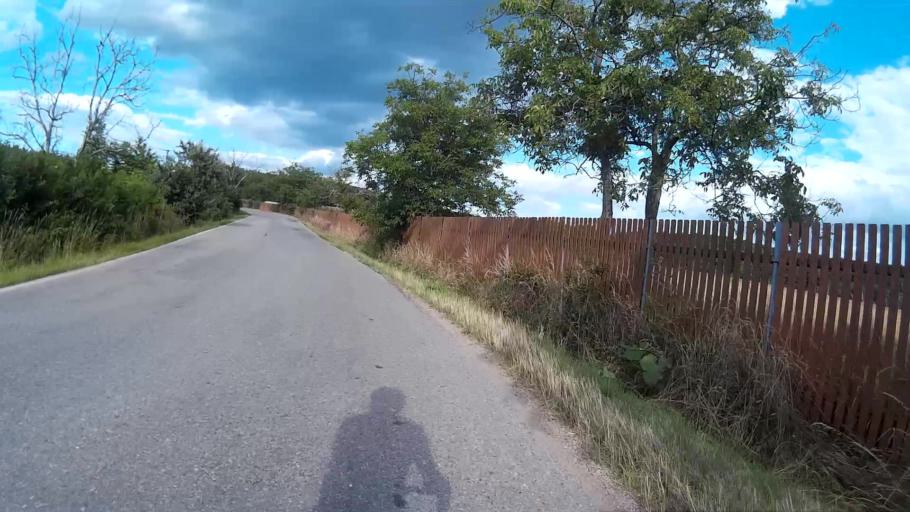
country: CZ
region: South Moravian
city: Ricany
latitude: 49.2057
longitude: 16.4291
